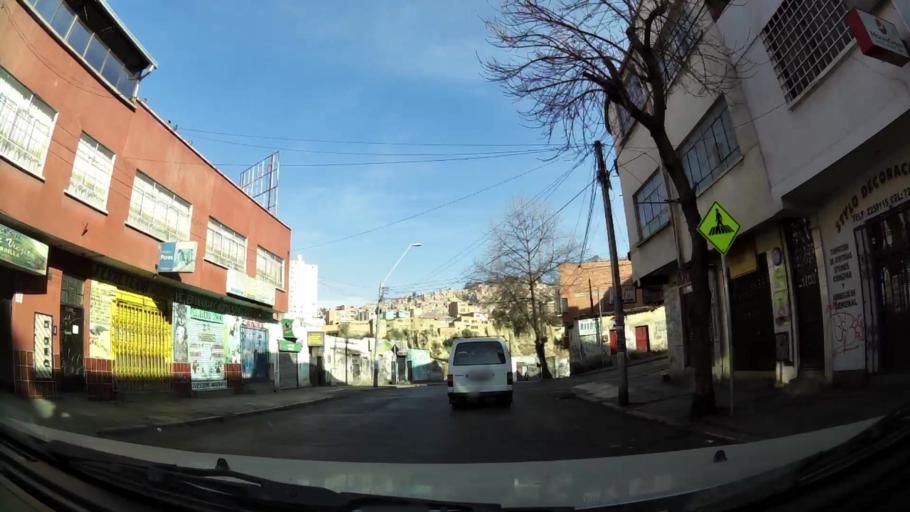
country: BO
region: La Paz
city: La Paz
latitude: -16.4956
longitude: -68.1176
